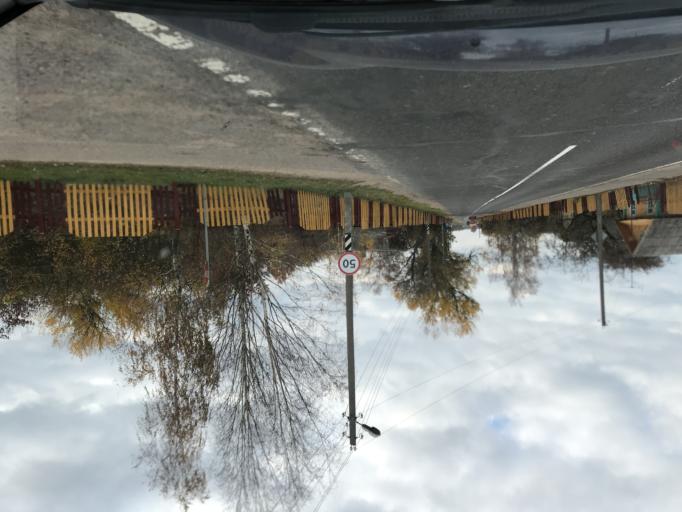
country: BY
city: Berezovka
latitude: 53.7414
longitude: 25.3568
